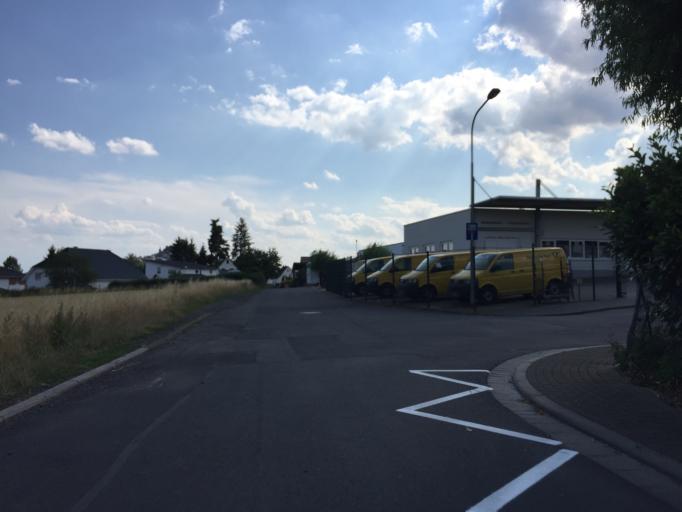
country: DE
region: Hesse
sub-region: Regierungsbezirk Giessen
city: Heuchelheim
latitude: 50.6295
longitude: 8.6399
